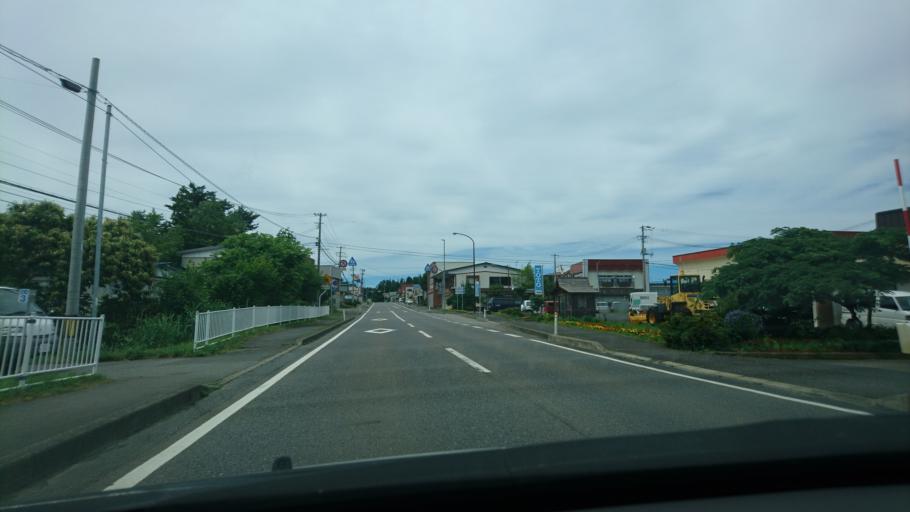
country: JP
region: Iwate
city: Miyako
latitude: 39.9227
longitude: 141.9013
